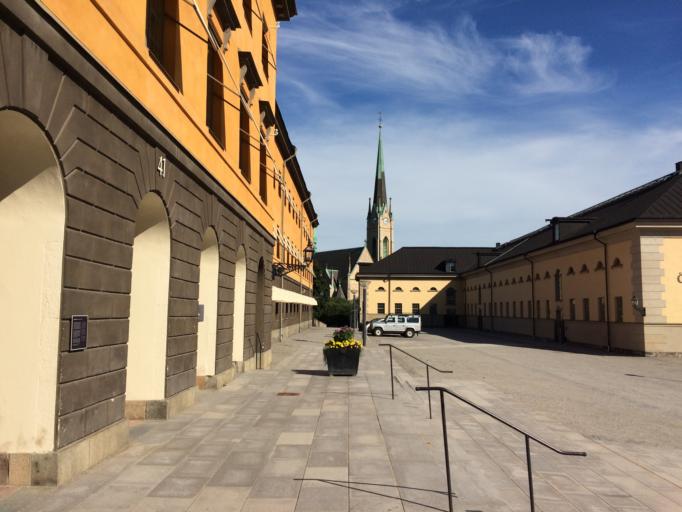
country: SE
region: Stockholm
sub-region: Stockholms Kommun
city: OEstermalm
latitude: 59.3341
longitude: 18.0900
